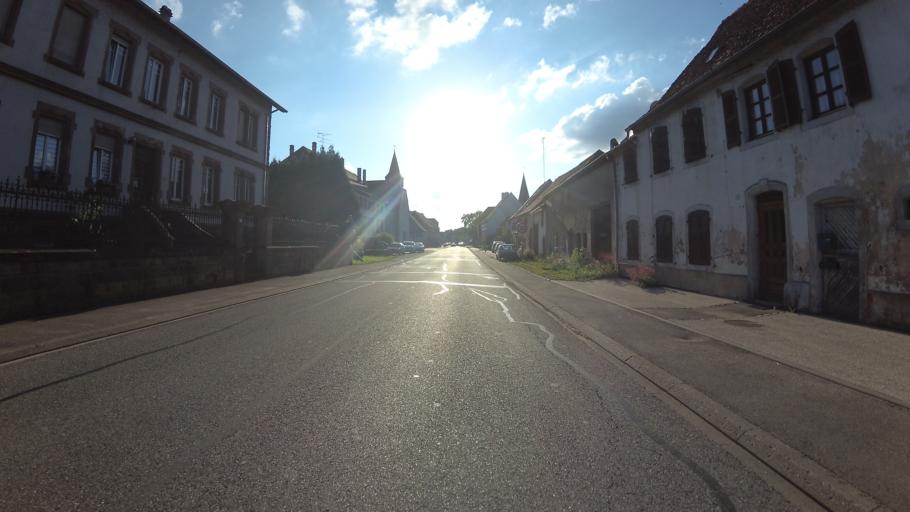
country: FR
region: Alsace
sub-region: Departement du Bas-Rhin
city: Diemeringen
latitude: 48.9520
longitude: 7.1786
